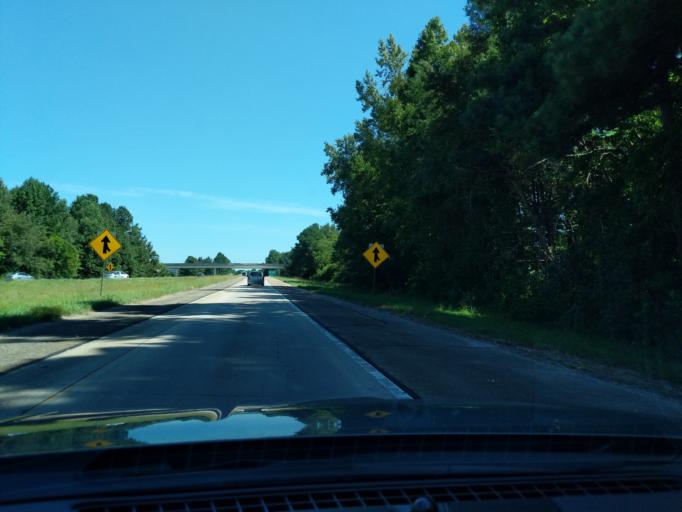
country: US
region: Georgia
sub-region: Habersham County
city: Cornelia
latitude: 34.5197
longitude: -83.5436
